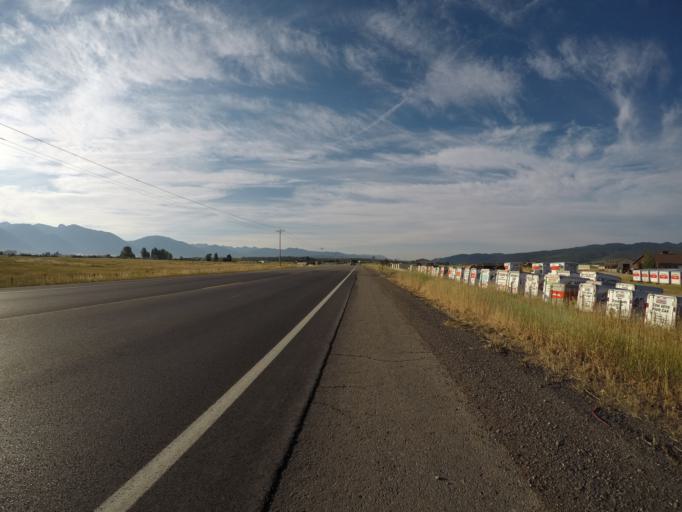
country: US
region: Wyoming
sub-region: Lincoln County
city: Afton
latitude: 42.9491
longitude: -111.0104
